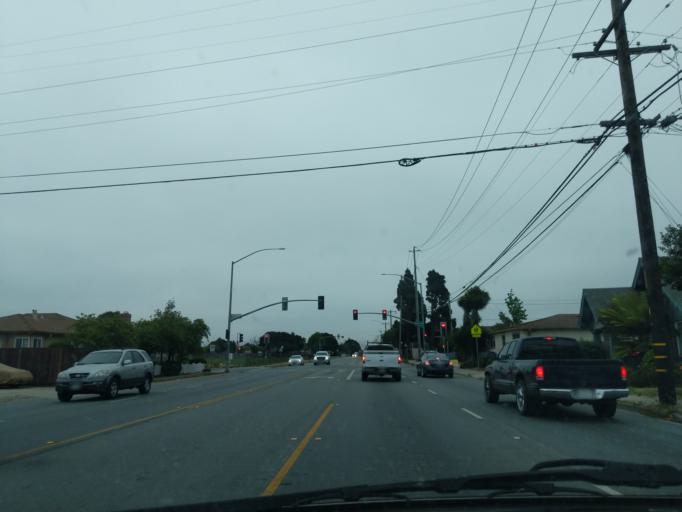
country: US
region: California
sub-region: Monterey County
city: Boronda
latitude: 36.6983
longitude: -121.6602
